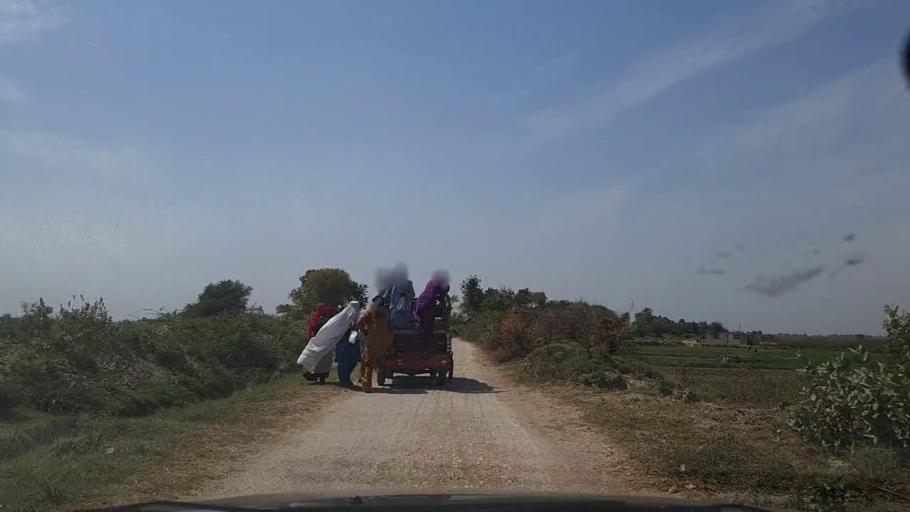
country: PK
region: Sindh
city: Mirpur Batoro
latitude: 24.6433
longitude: 68.1463
